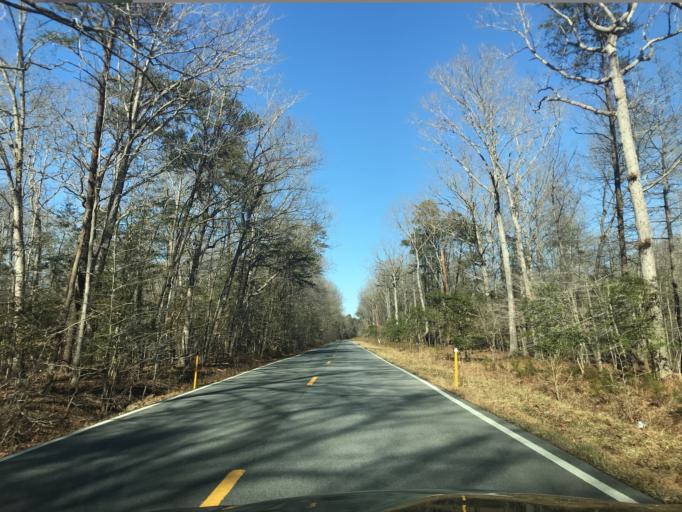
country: US
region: Virginia
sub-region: Prince William County
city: Quantico Station
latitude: 38.4818
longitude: -77.2558
